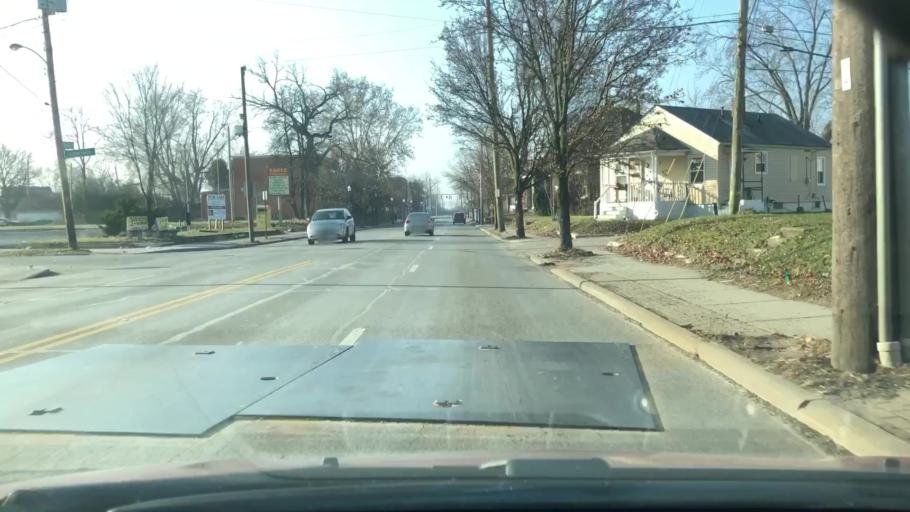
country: US
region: Ohio
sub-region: Franklin County
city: Columbus
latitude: 39.9957
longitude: -82.9798
